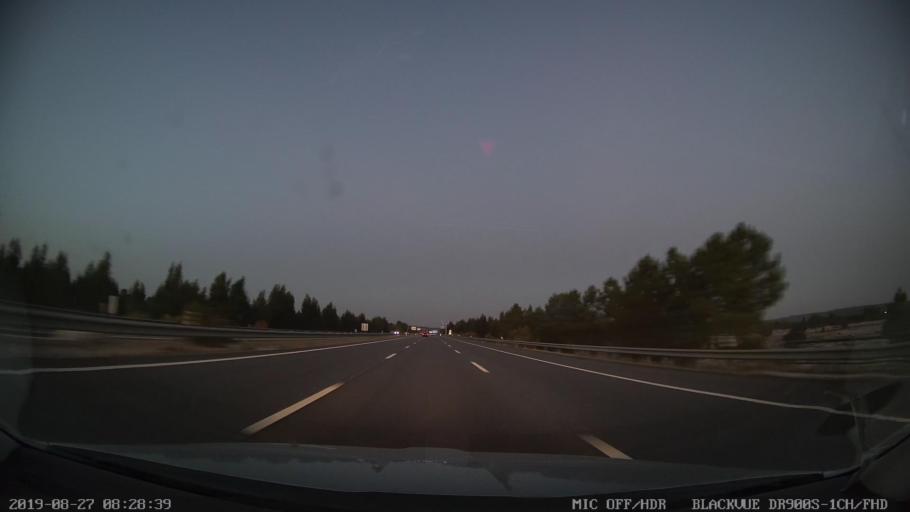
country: PT
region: Evora
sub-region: Vendas Novas
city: Vendas Novas
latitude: 38.6008
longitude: -8.6709
